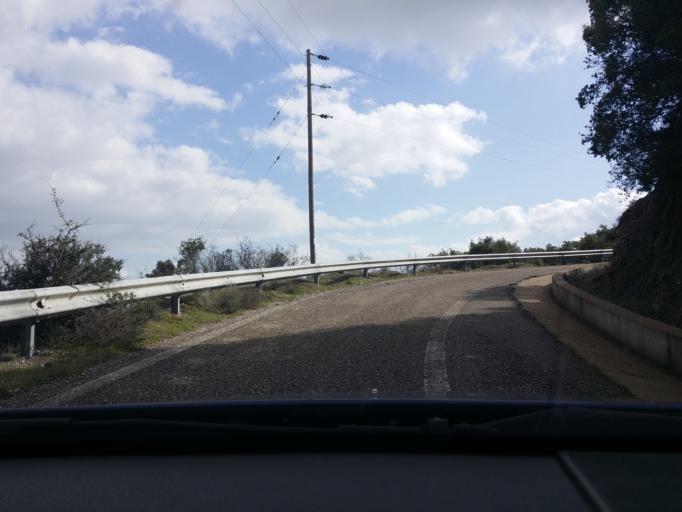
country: GR
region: West Greece
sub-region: Nomos Aitolias kai Akarnanias
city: Fitiai
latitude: 38.6574
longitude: 21.1973
